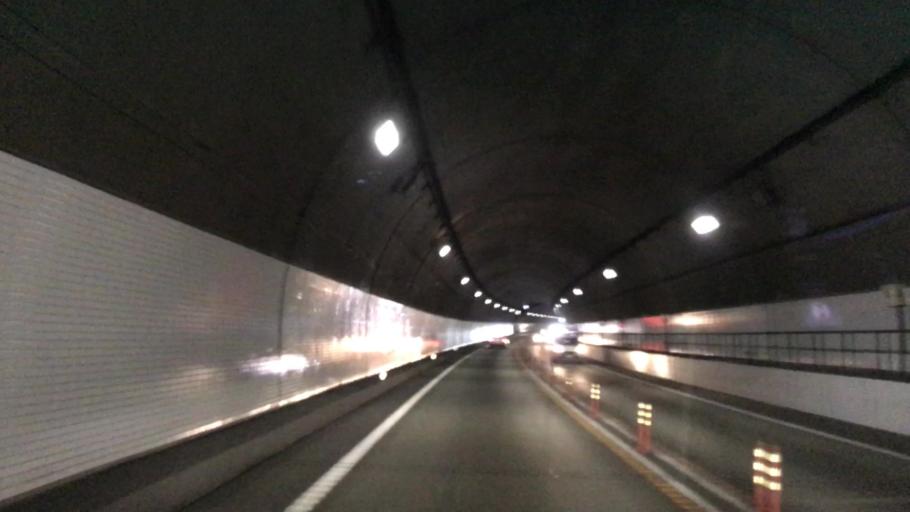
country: JP
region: Hokkaido
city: Iwamizawa
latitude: 42.9339
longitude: 142.1000
